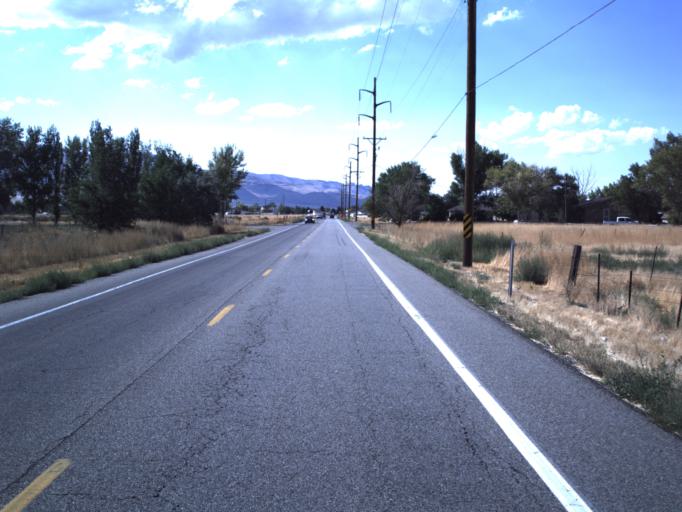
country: US
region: Utah
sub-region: Tooele County
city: Grantsville
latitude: 40.5887
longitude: -112.4163
